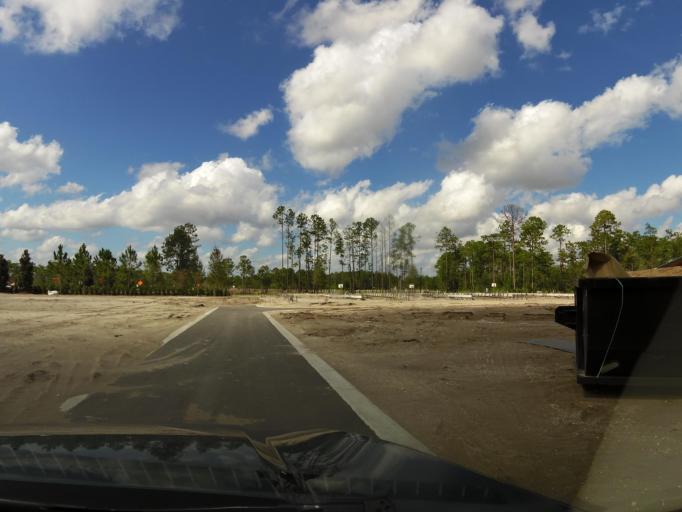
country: US
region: Florida
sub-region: Saint Johns County
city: Ponte Vedra Beach
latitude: 30.2461
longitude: -81.4974
